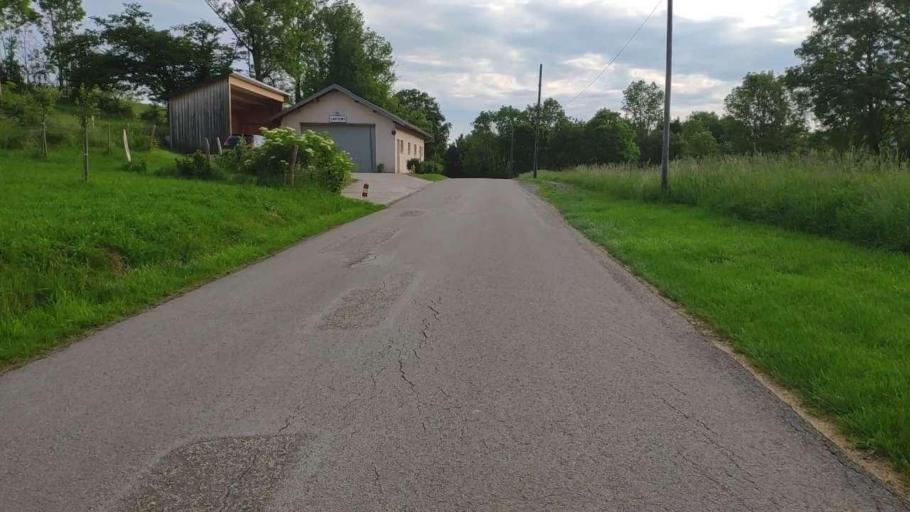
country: FR
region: Franche-Comte
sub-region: Departement du Jura
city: Perrigny
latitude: 46.7179
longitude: 5.5932
